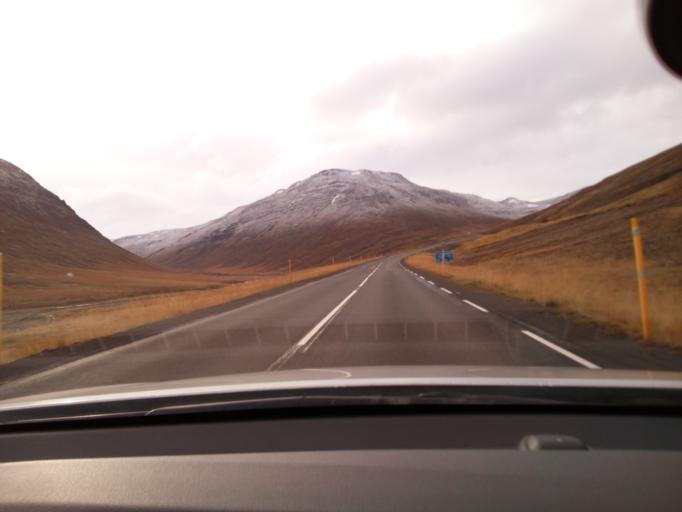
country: IS
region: Northeast
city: Dalvik
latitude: 65.4835
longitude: -18.6512
